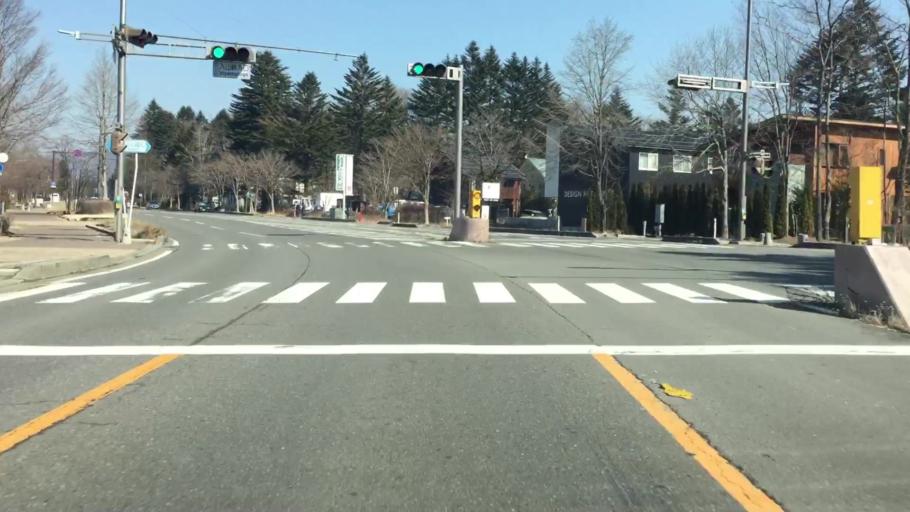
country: JP
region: Nagano
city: Saku
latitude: 36.3329
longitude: 138.6315
